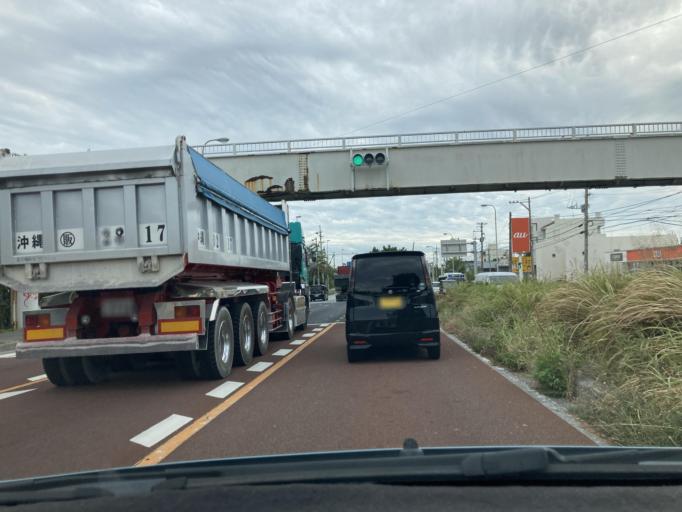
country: JP
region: Okinawa
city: Okinawa
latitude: 26.3834
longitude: 127.7555
